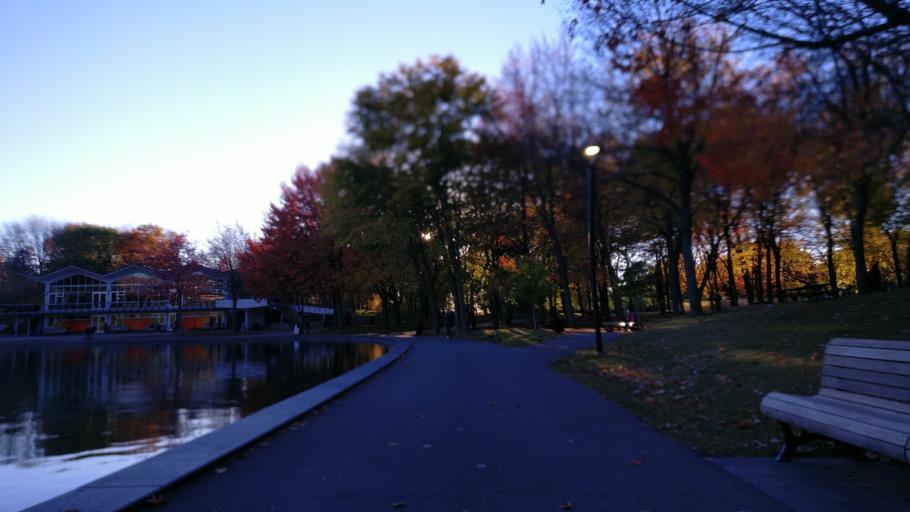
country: CA
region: Quebec
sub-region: Montreal
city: Montreal
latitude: 45.4992
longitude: -73.5981
